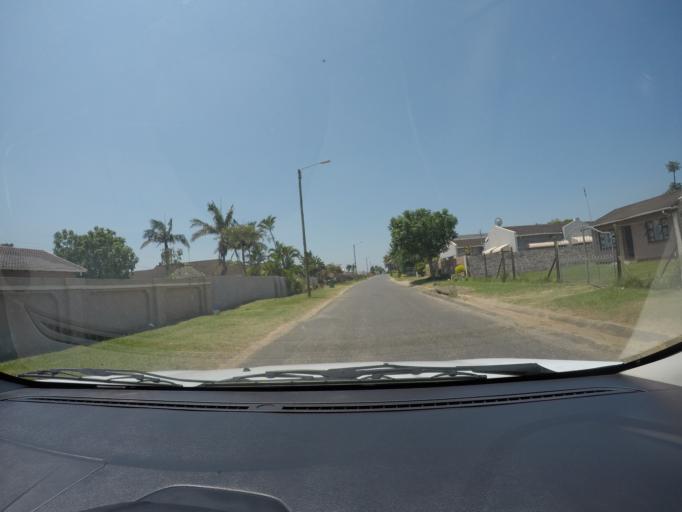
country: ZA
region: KwaZulu-Natal
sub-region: uThungulu District Municipality
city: eSikhawini
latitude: -28.8895
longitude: 31.8820
